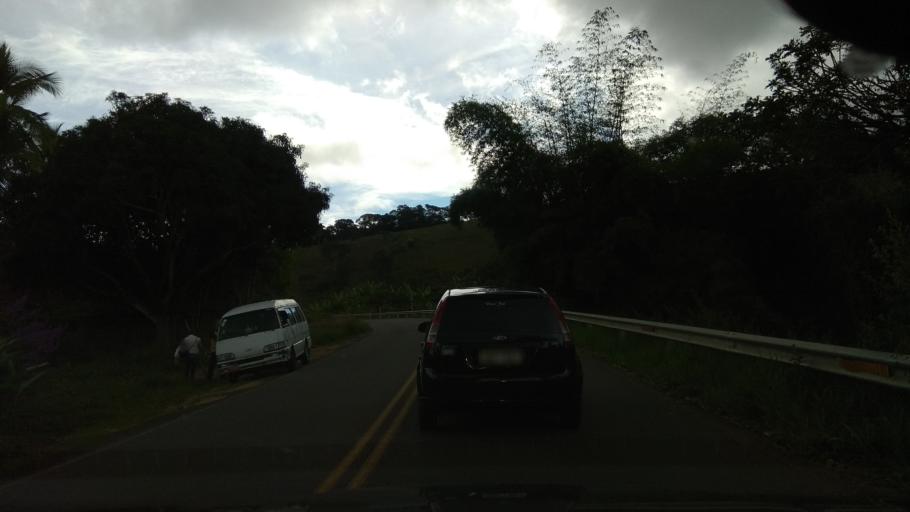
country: BR
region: Bahia
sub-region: Mutuipe
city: Mutuipe
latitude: -13.2406
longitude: -39.5377
